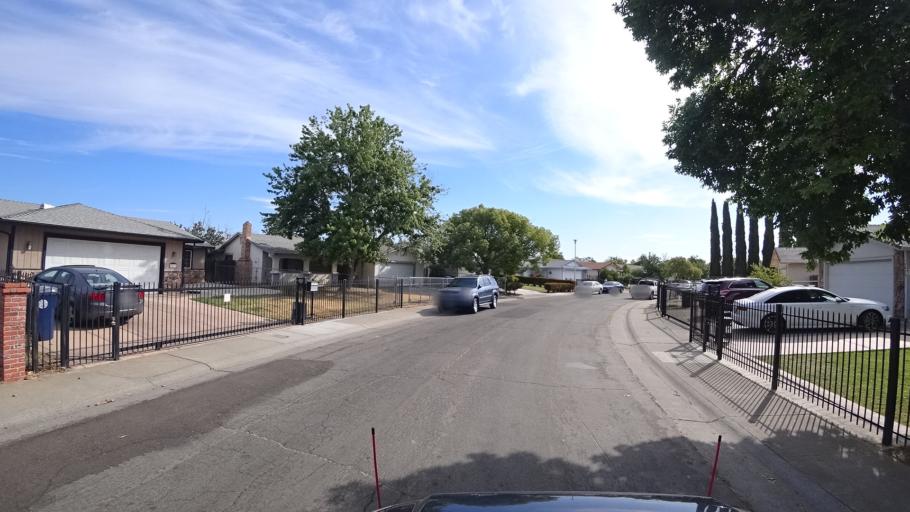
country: US
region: California
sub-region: Sacramento County
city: Florin
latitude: 38.5146
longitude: -121.4179
